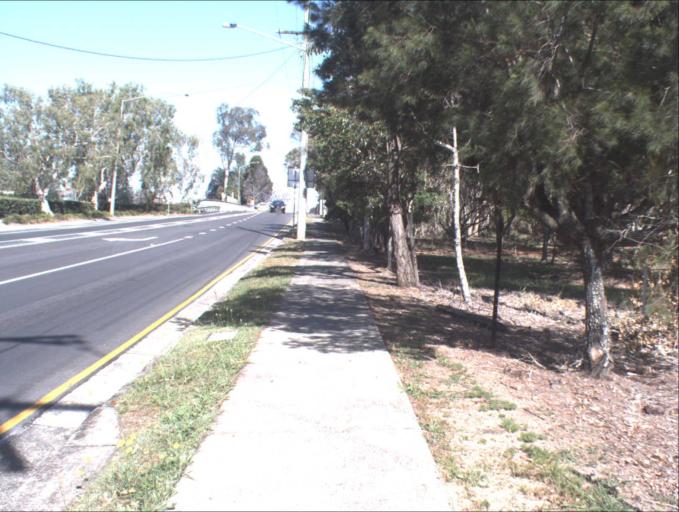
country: AU
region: Queensland
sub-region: Logan
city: Rochedale South
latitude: -27.5941
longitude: 153.1125
